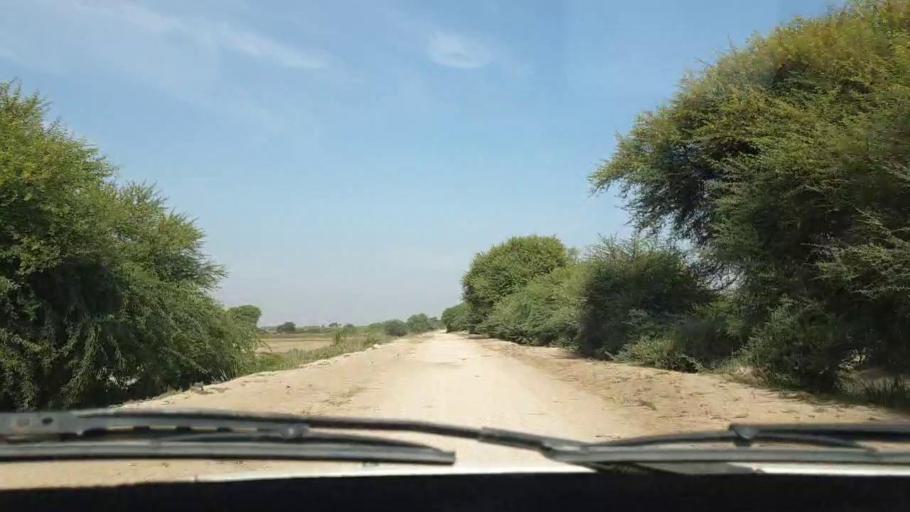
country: PK
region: Sindh
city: Bulri
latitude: 24.8959
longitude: 68.4624
